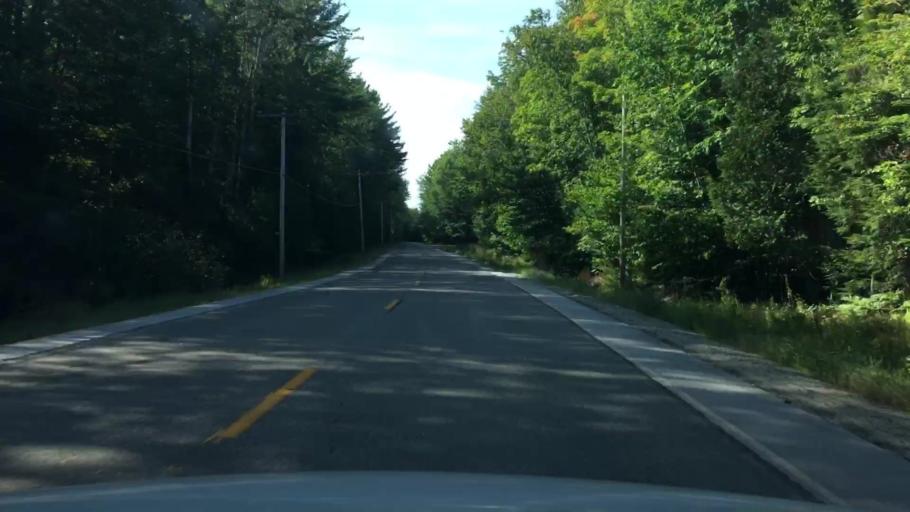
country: US
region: Maine
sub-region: Penobscot County
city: Enfield
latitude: 45.2153
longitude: -68.5289
